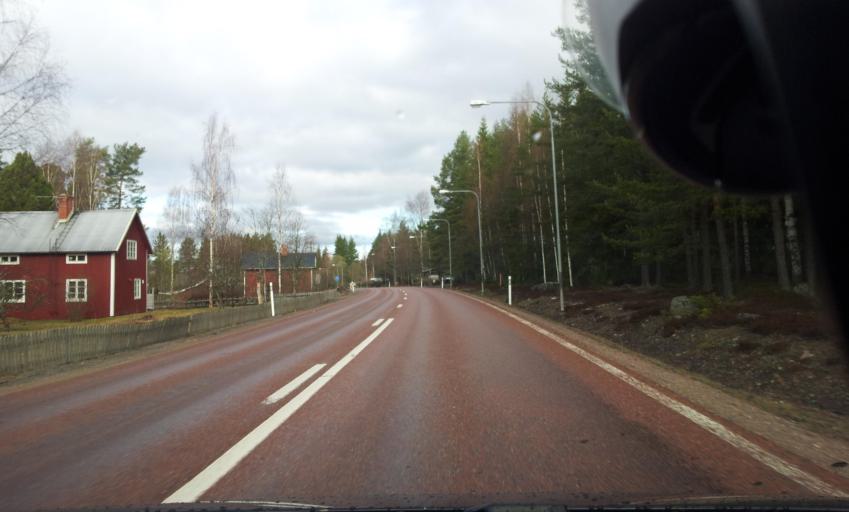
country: SE
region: Gaevleborg
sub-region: Ljusdals Kommun
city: Ljusdal
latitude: 61.8243
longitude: 16.1449
